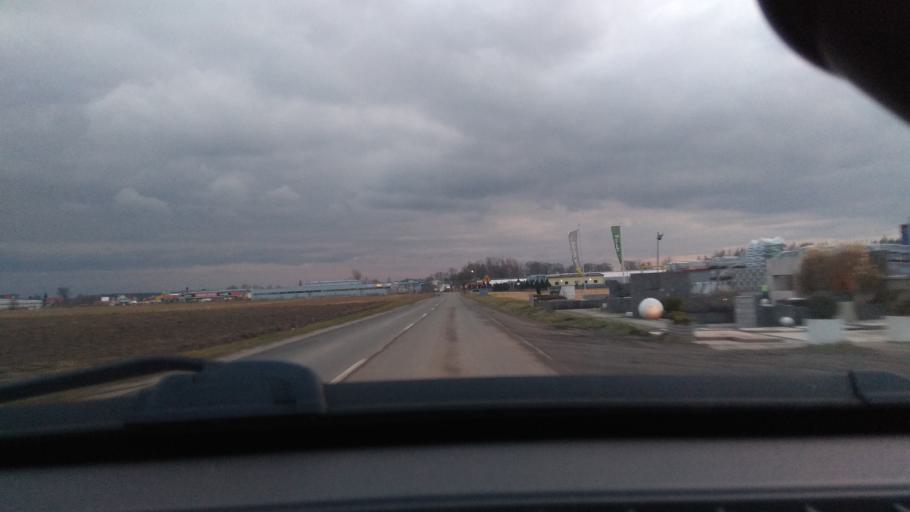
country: PL
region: Greater Poland Voivodeship
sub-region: Powiat kepinski
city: Kepno
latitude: 51.2917
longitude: 18.0061
